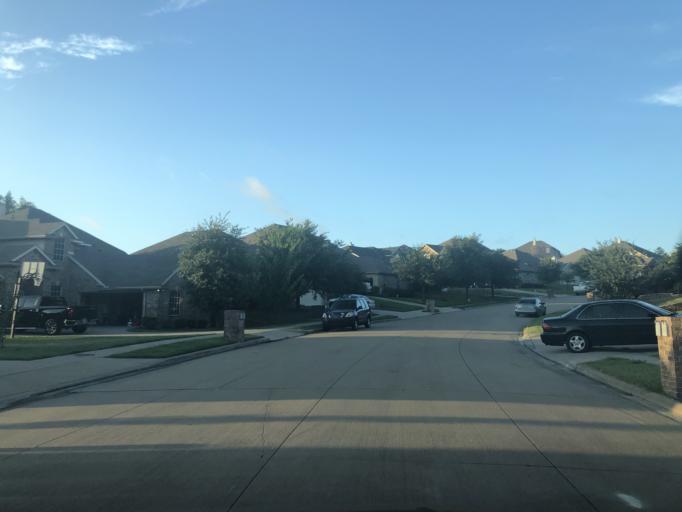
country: US
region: Texas
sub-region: Dallas County
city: Duncanville
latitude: 32.6548
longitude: -96.9684
